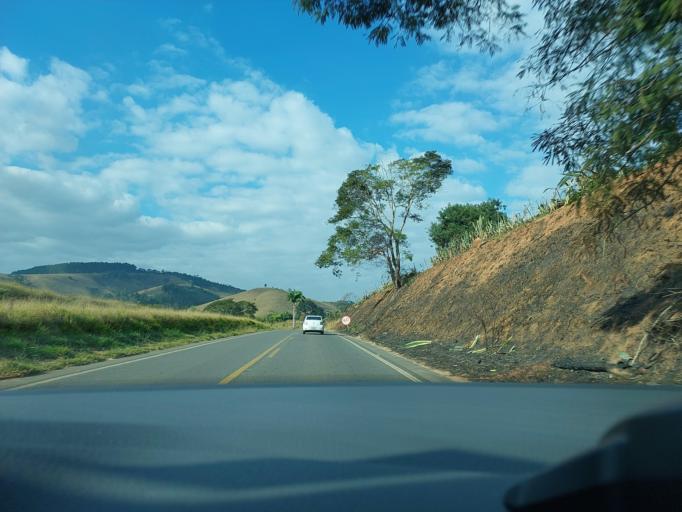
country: BR
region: Minas Gerais
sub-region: Vicosa
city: Vicosa
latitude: -20.8271
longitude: -42.7757
